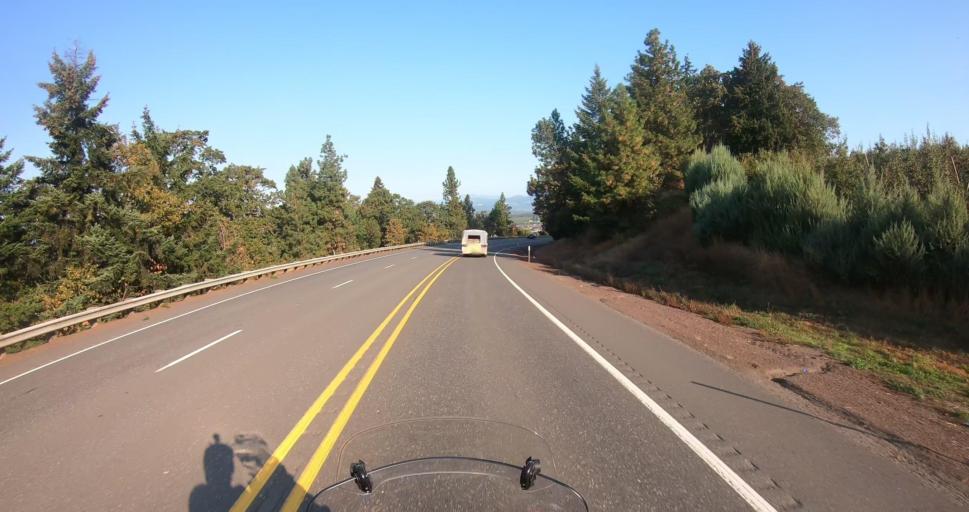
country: US
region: Oregon
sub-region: Hood River County
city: Odell
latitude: 45.6174
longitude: -121.5315
